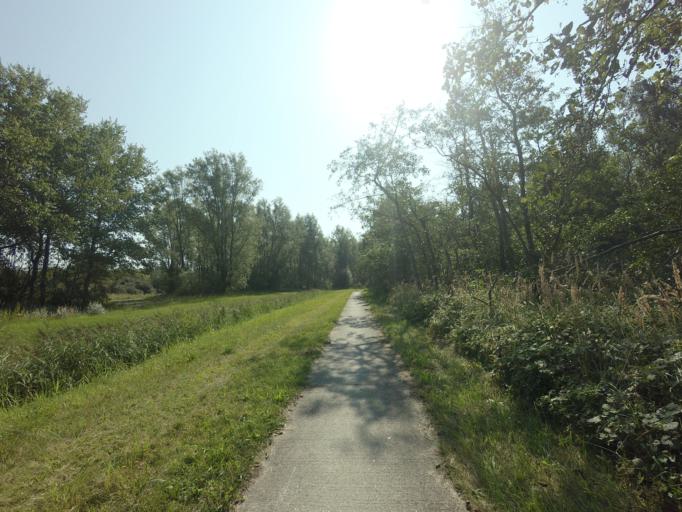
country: NL
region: Groningen
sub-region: Gemeente De Marne
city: Ulrum
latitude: 53.3922
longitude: 6.2563
